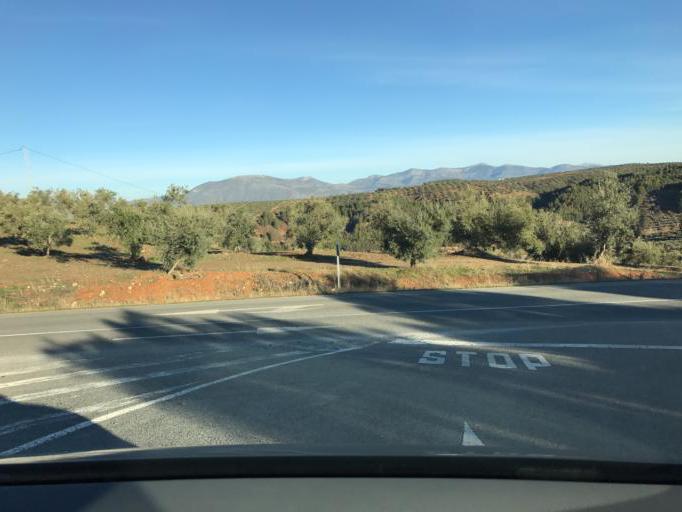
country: ES
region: Andalusia
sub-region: Provincia de Granada
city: Calicasas
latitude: 37.2661
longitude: -3.6335
